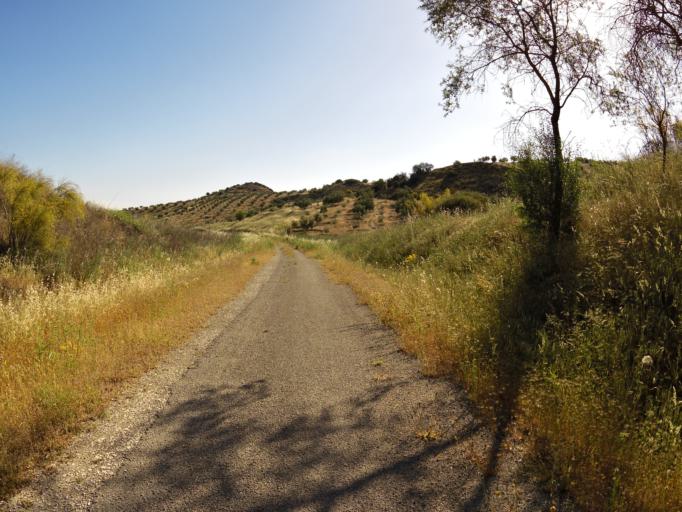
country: ES
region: Andalusia
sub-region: Province of Cordoba
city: Fuente-Tojar
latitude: 37.5793
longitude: -4.1792
